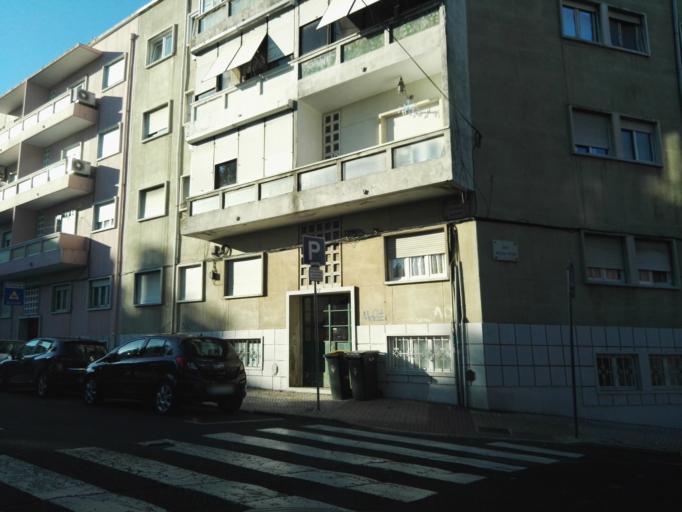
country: PT
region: Lisbon
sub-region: Lisbon
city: Lisbon
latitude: 38.7480
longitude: -9.1361
